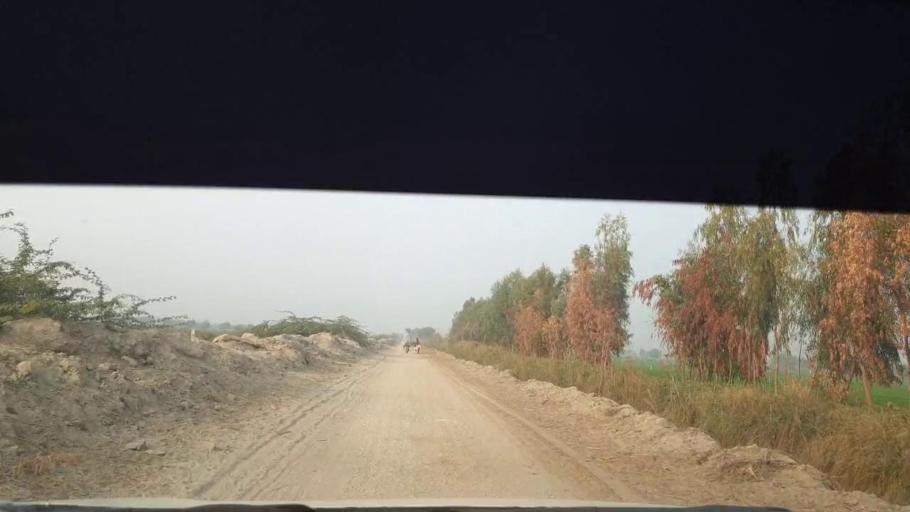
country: PK
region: Sindh
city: Berani
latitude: 25.8327
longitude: 68.8913
